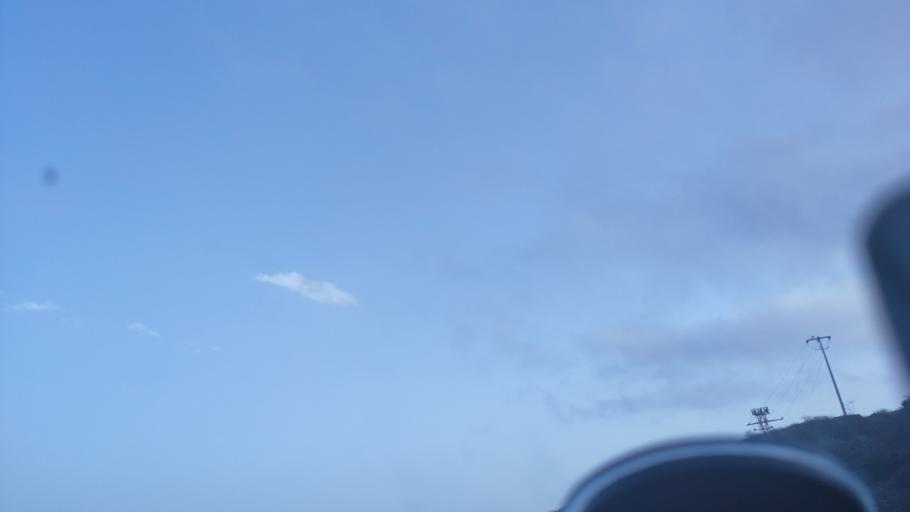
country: CV
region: Mosteiros
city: Porto dos Mosteiros
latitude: 15.0109
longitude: -24.3061
